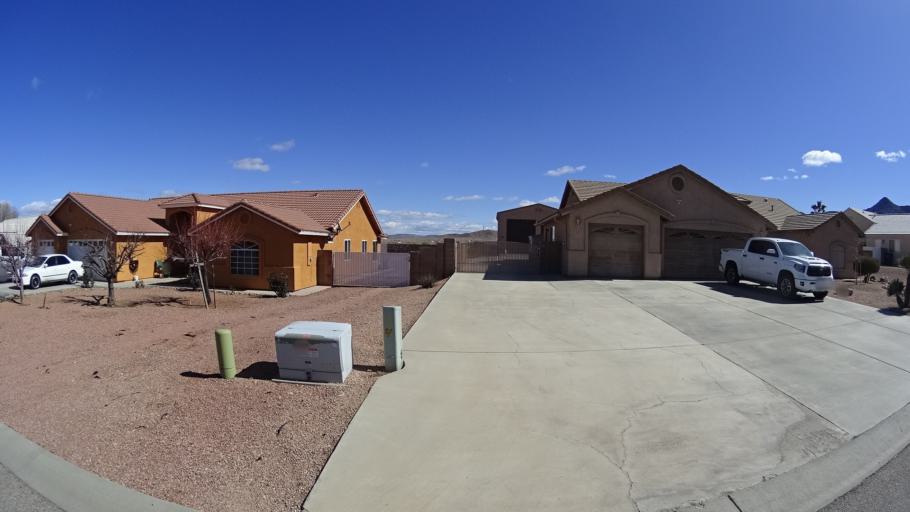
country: US
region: Arizona
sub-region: Mohave County
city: Kingman
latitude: 35.2010
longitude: -113.9594
